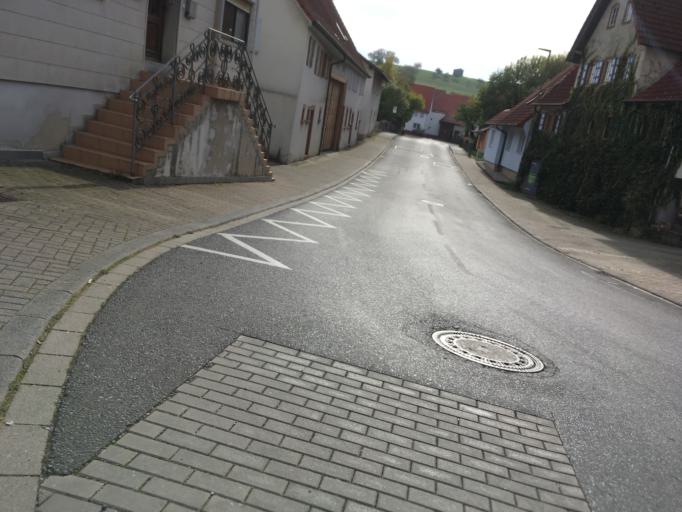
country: DE
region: Baden-Wuerttemberg
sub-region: Karlsruhe Region
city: Rosenberg
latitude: 49.4884
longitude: 9.4543
